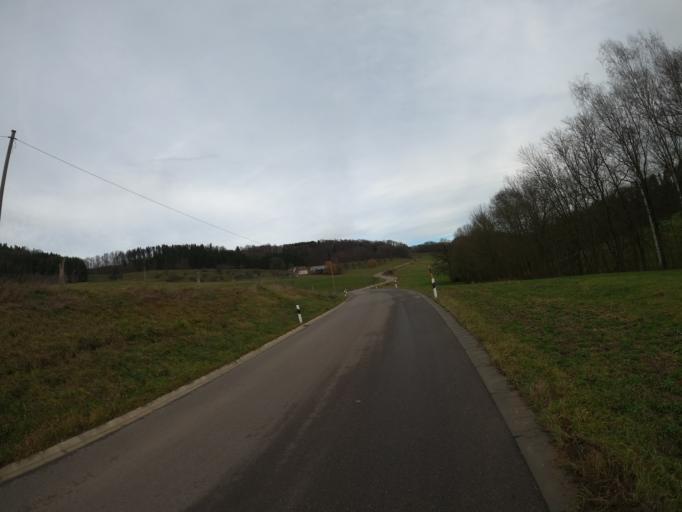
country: DE
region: Baden-Wuerttemberg
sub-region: Regierungsbezirk Stuttgart
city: Ottenbach
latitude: 48.7477
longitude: 9.7564
